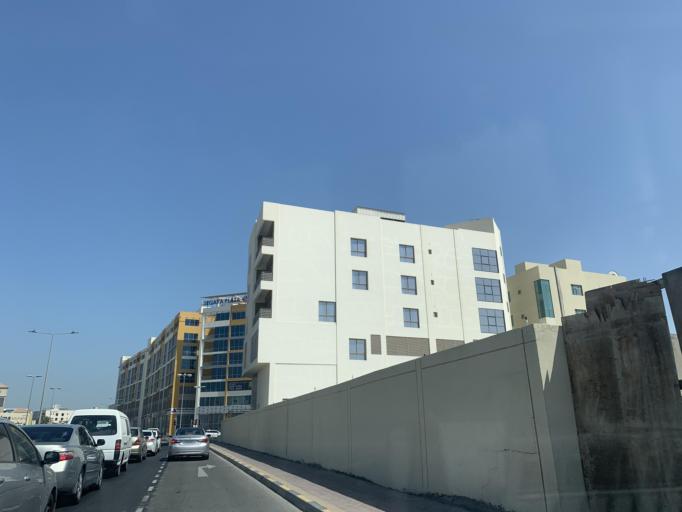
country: BH
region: Manama
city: Manama
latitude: 26.2124
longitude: 50.5745
